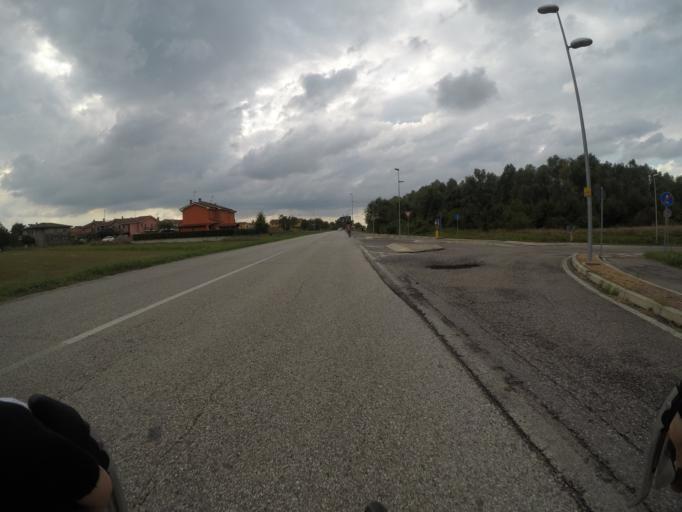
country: IT
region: Veneto
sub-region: Provincia di Rovigo
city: Polesella
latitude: 44.9578
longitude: 11.7323
